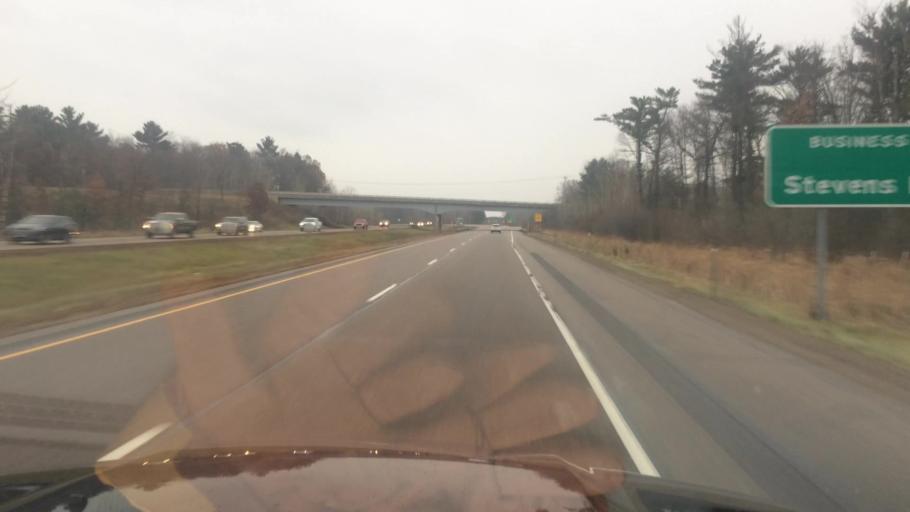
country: US
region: Wisconsin
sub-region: Portage County
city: Stevens Point
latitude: 44.5542
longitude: -89.5854
